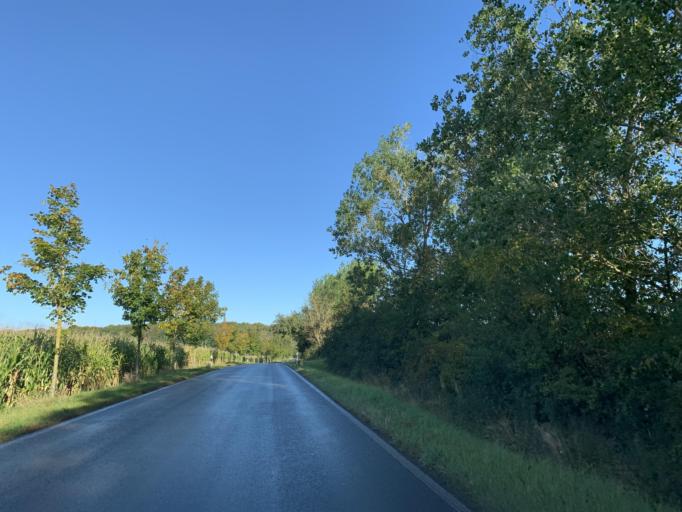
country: DE
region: Mecklenburg-Vorpommern
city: Burg Stargard
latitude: 53.4934
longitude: 13.2663
